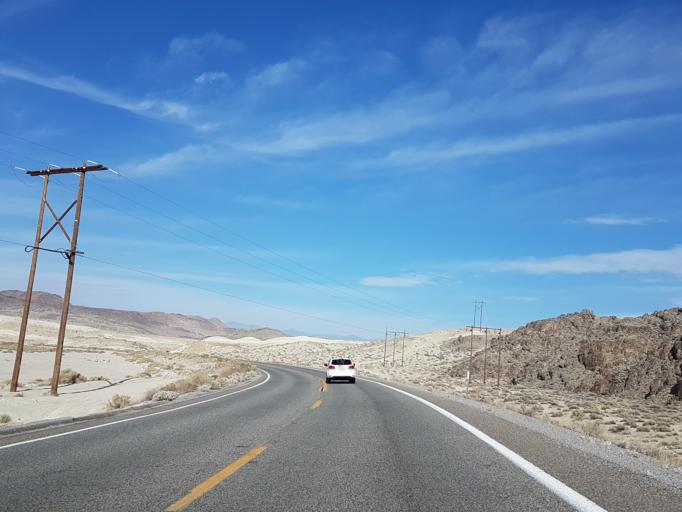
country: US
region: California
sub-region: San Bernardino County
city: Searles Valley
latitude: 35.6632
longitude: -117.4286
